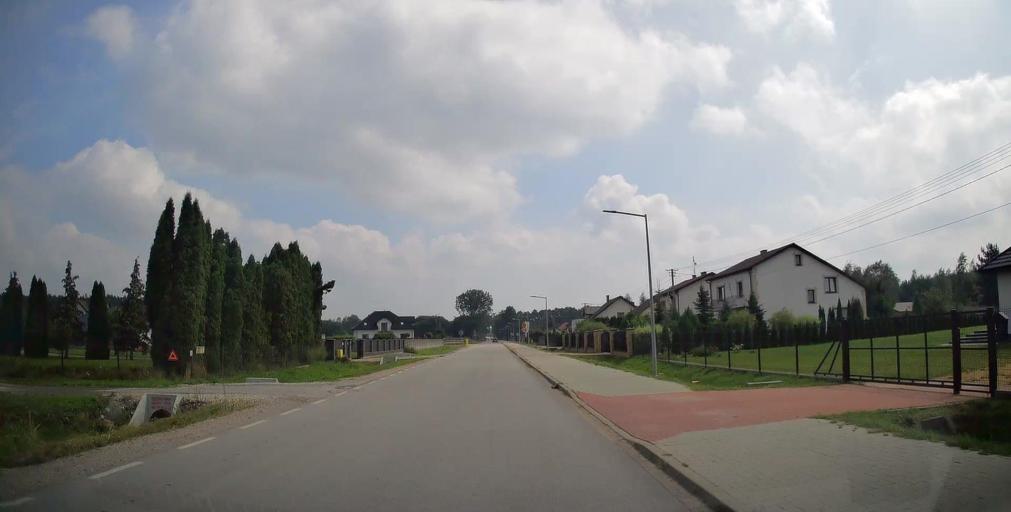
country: PL
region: Masovian Voivodeship
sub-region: Powiat bialobrzeski
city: Sucha
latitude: 51.6163
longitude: 20.9590
